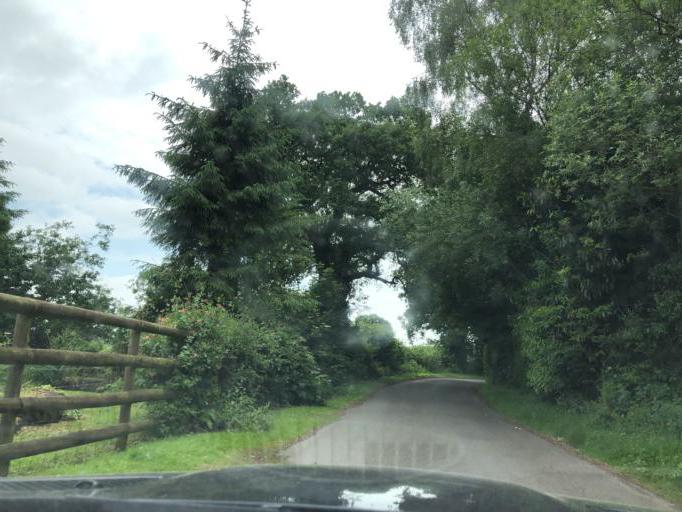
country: GB
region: England
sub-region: Warwickshire
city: Wroxall
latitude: 52.3420
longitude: -1.6446
